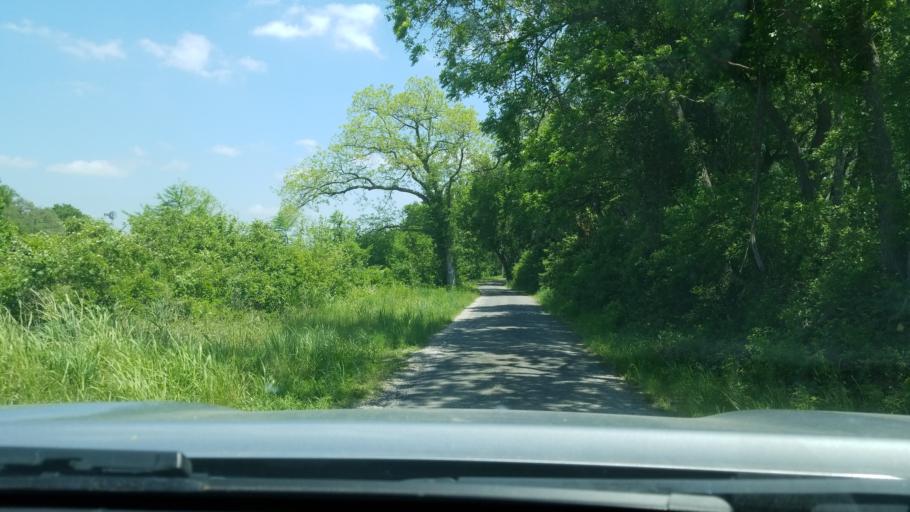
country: US
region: Texas
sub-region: Blanco County
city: Blanco
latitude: 30.0904
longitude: -98.4011
